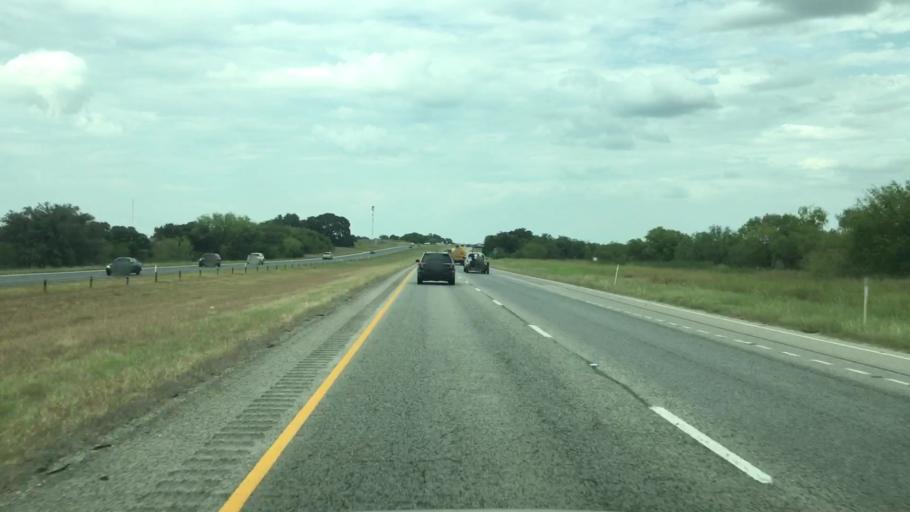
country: US
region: Texas
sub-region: Atascosa County
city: Pleasanton
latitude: 29.1130
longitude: -98.4320
